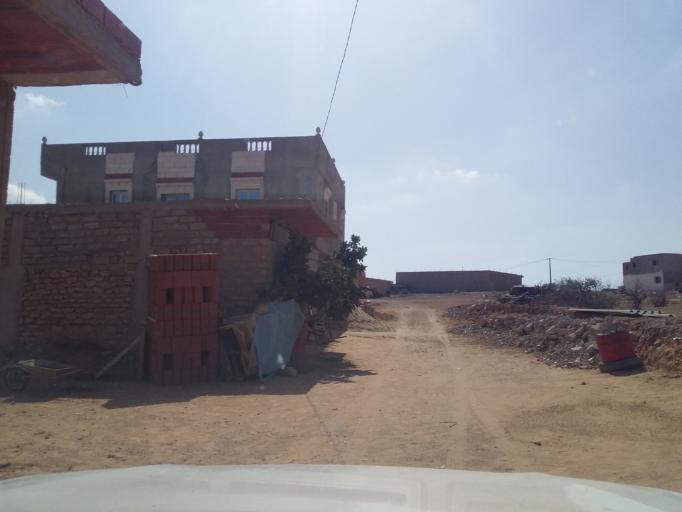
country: TN
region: Madanin
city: Medenine
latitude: 33.5812
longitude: 10.3218
